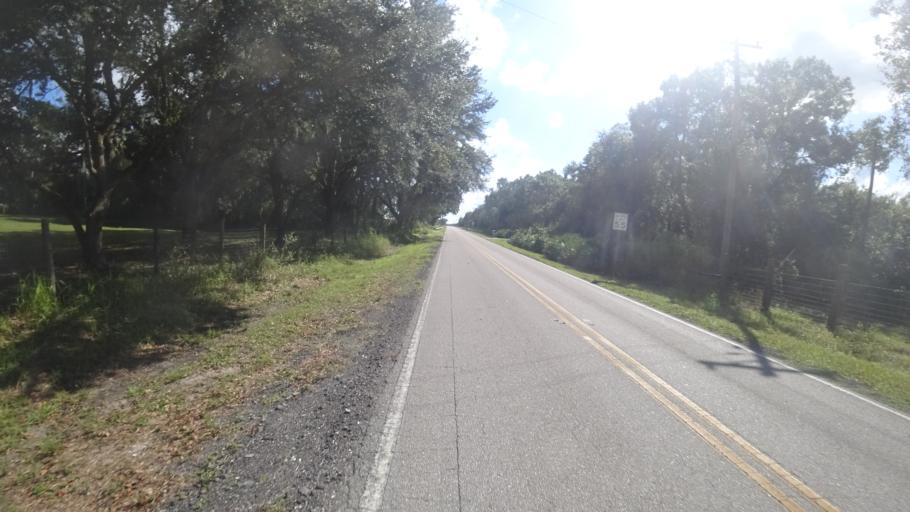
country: US
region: Florida
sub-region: Hillsborough County
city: Wimauma
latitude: 27.4275
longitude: -82.1331
